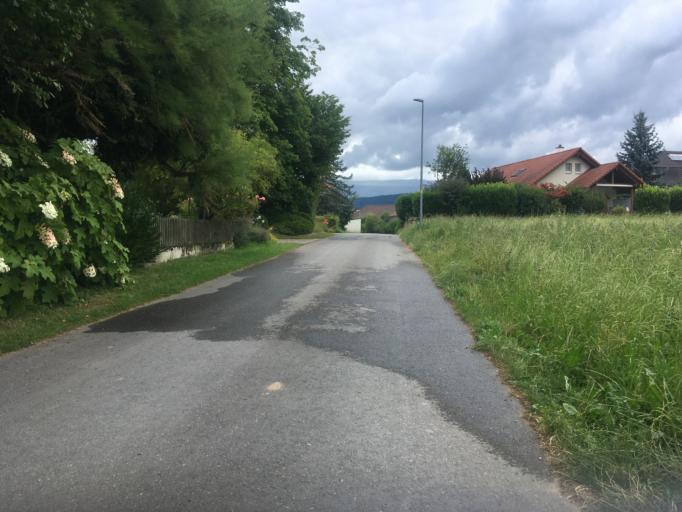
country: CH
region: Bern
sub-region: Seeland District
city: Erlach
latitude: 47.0305
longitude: 7.1136
